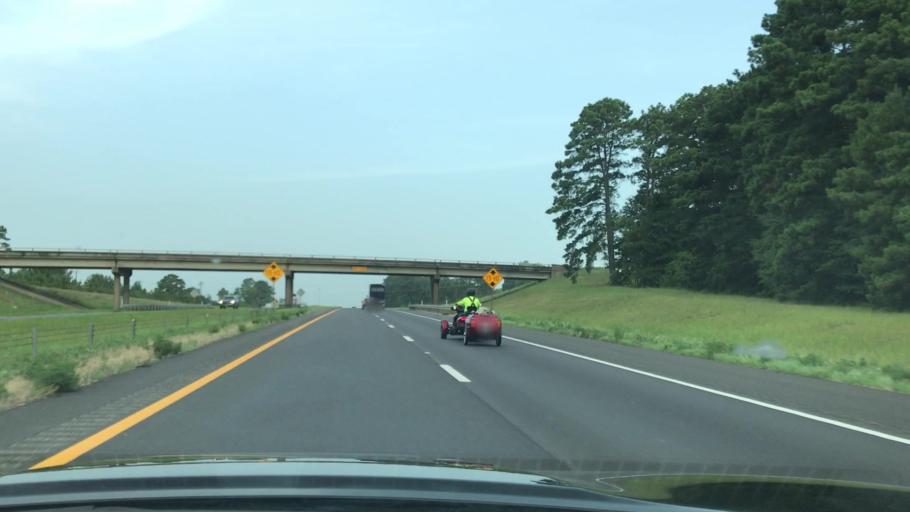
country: US
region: Texas
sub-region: Harrison County
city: Hallsville
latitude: 32.4670
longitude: -94.6202
